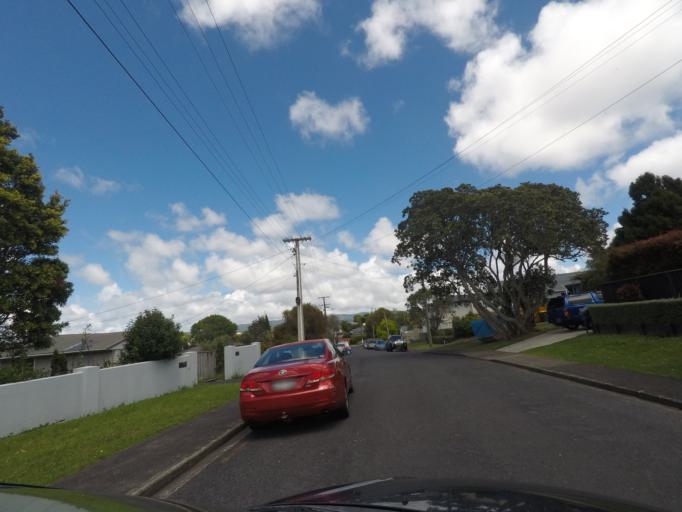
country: NZ
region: Auckland
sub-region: Auckland
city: Rosebank
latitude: -36.8710
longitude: 174.6497
